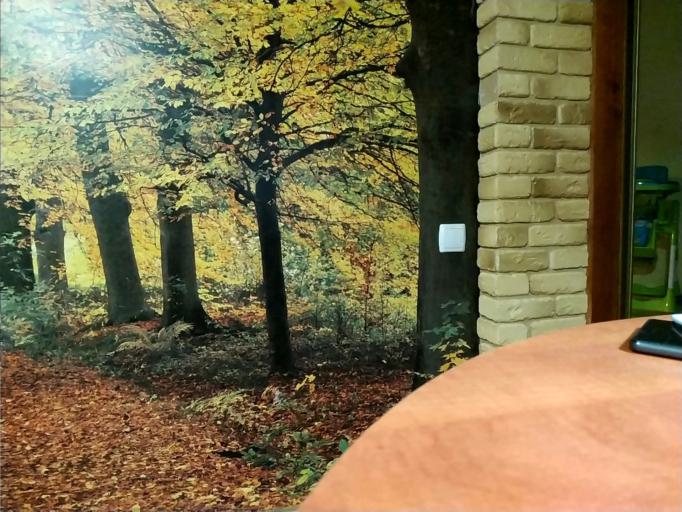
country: BY
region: Minsk
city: Plyeshchanitsy
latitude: 54.4289
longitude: 27.6467
